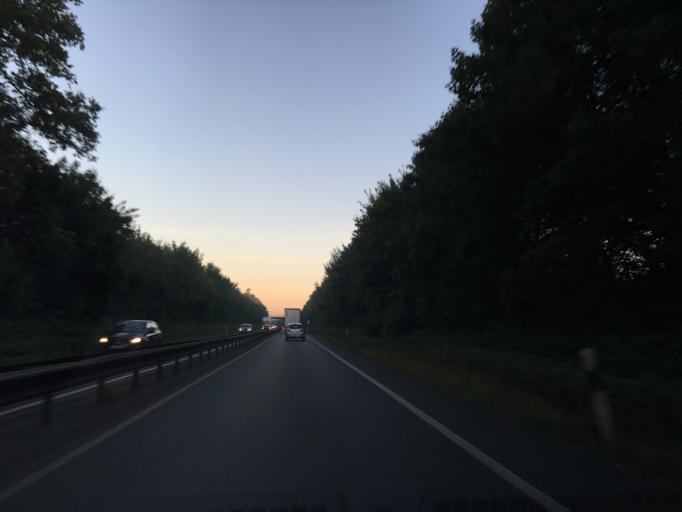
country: DE
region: North Rhine-Westphalia
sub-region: Regierungsbezirk Munster
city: Altenberge
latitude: 52.0181
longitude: 7.4972
